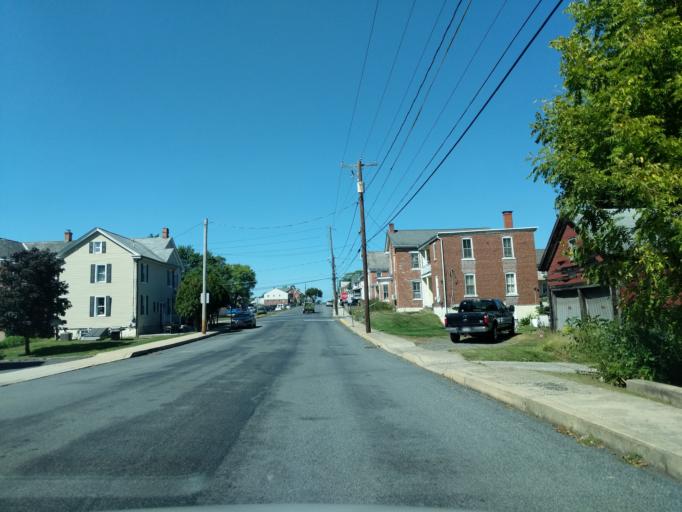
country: US
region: Pennsylvania
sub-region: Montgomery County
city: East Greenville
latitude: 40.4022
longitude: -75.5068
